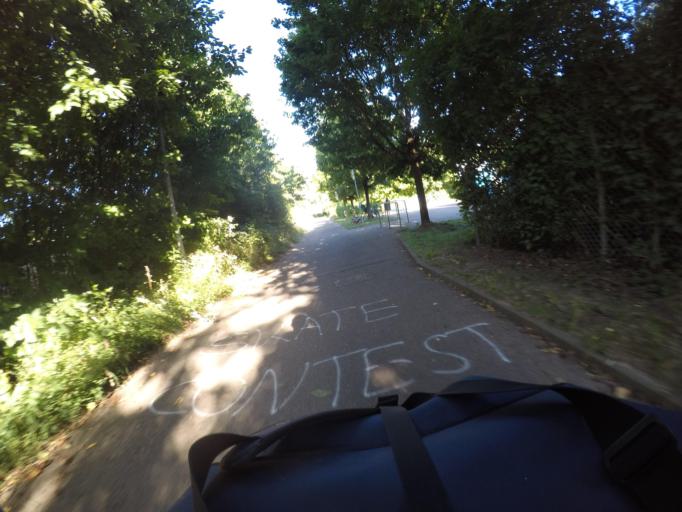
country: DE
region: Baden-Wuerttemberg
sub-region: Regierungsbezirk Stuttgart
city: Ludwigsburg
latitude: 48.8910
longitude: 9.2166
